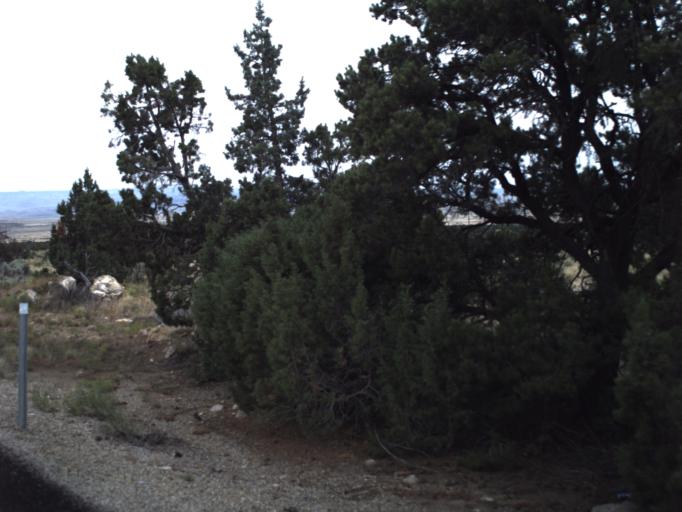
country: US
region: Utah
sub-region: Carbon County
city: East Carbon City
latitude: 39.5243
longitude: -110.3982
